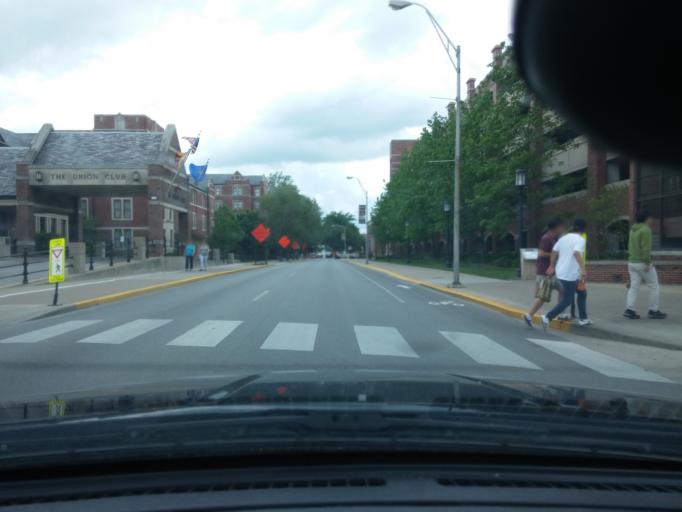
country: US
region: Indiana
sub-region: Tippecanoe County
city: West Lafayette
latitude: 40.4246
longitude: -86.9104
